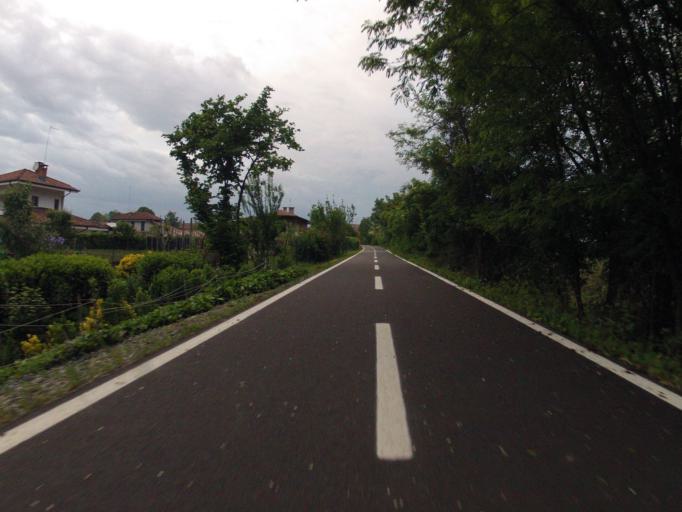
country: IT
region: Piedmont
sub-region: Provincia di Torino
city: Villafranca Piemonte
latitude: 44.7837
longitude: 7.5105
